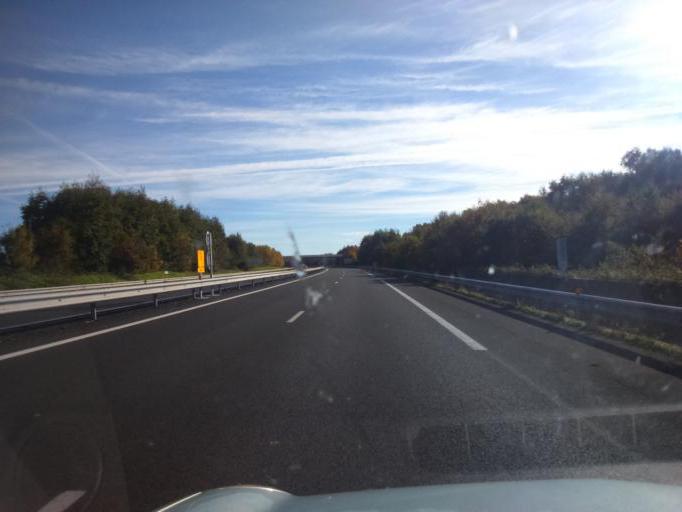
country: FR
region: Poitou-Charentes
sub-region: Departement de la Charente-Maritime
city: Tonnay-Charente
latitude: 45.9549
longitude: -0.9032
